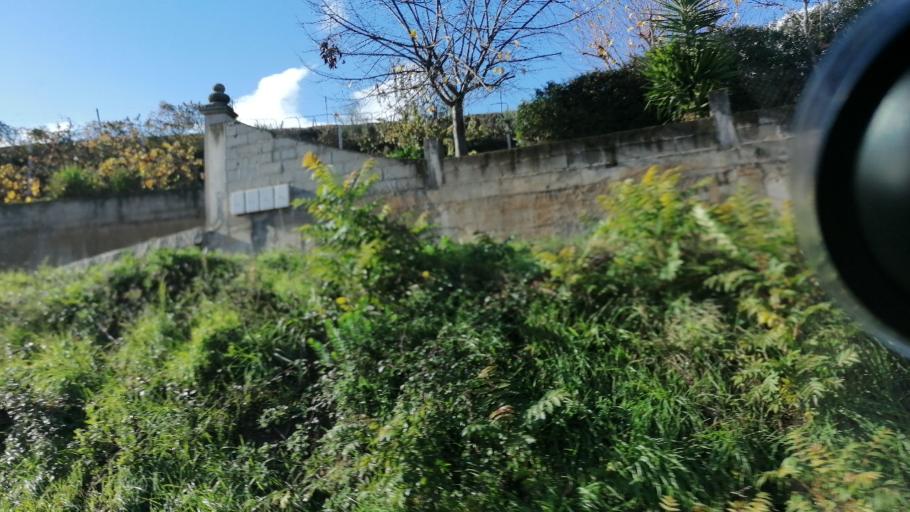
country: PT
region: Viseu
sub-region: Lamego
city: Lamego
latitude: 41.1230
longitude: -7.7927
